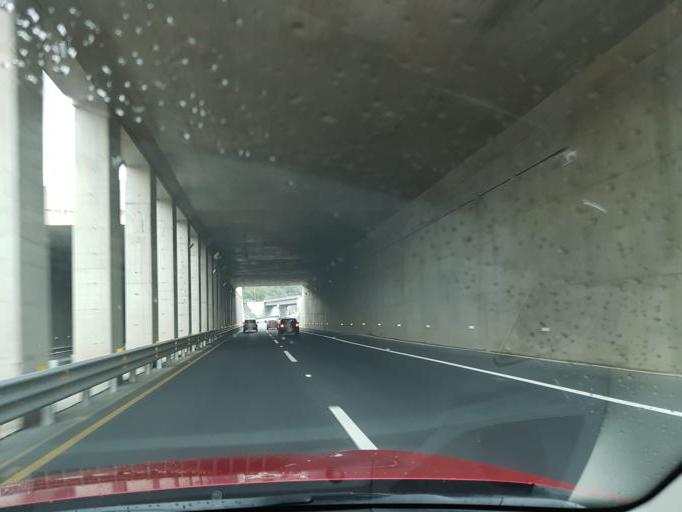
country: MX
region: Morelos
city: San Jeronimo Acazulco
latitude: 19.2969
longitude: -99.4129
